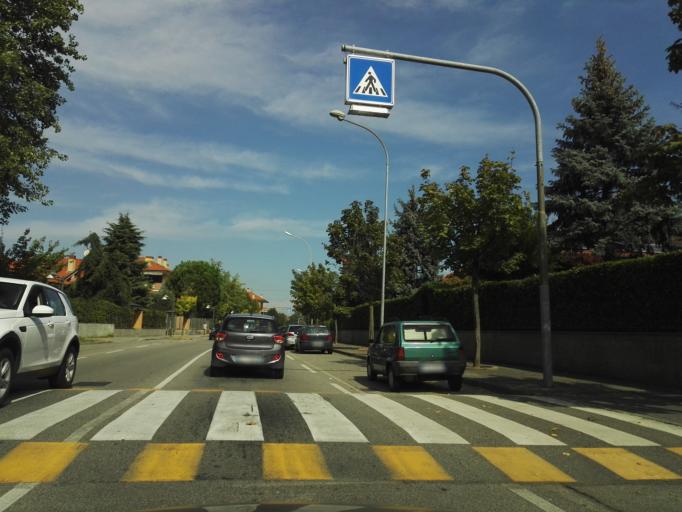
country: IT
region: Lombardy
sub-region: Citta metropolitana di Milano
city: Bettola-Zeloforomagno
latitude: 45.4311
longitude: 9.3069
